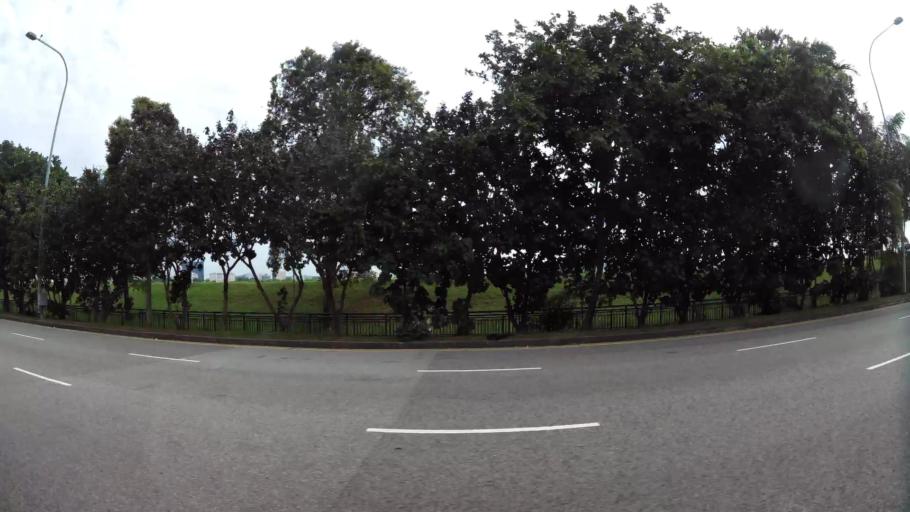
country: SG
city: Singapore
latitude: 1.3088
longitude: 103.7391
